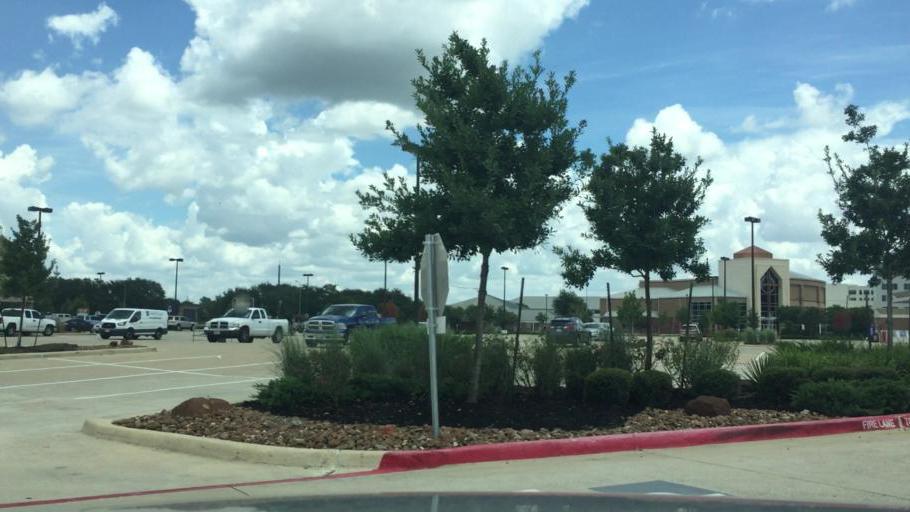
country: US
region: Texas
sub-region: Harris County
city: Cypress
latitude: 29.9890
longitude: -95.7375
